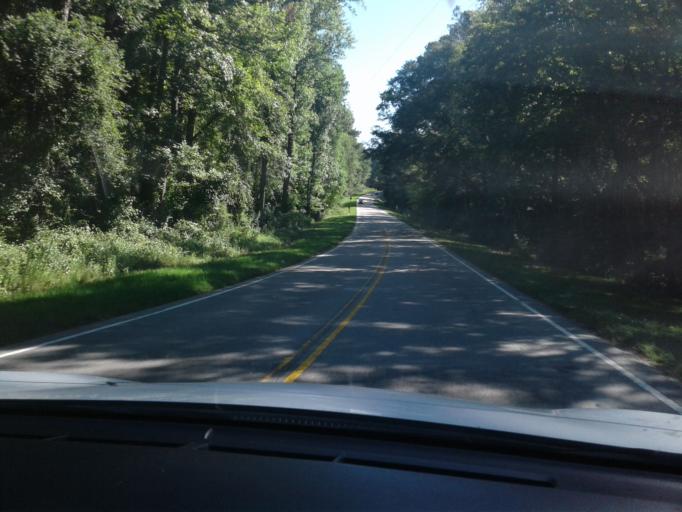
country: US
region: North Carolina
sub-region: Harnett County
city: Lillington
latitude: 35.3592
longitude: -78.9004
